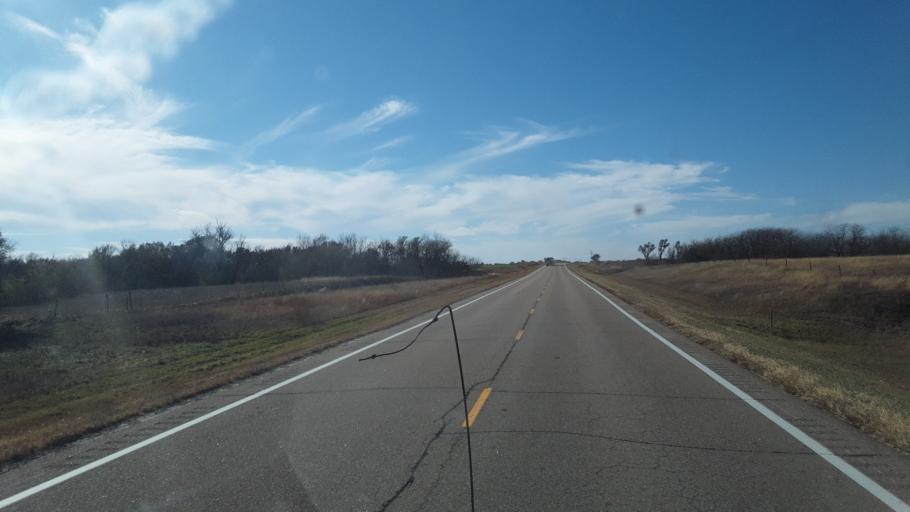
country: US
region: Kansas
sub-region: Pawnee County
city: Larned
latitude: 38.1895
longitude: -99.3027
